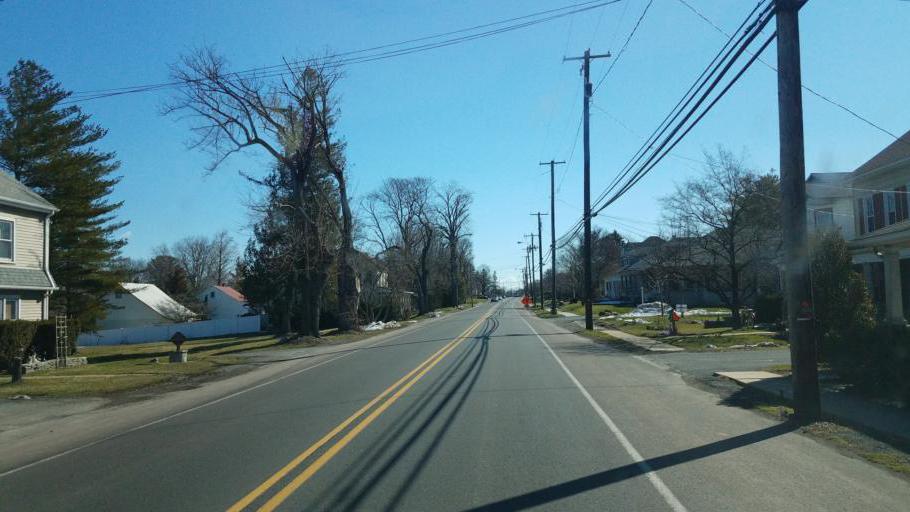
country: US
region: Pennsylvania
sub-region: Lancaster County
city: Brownstown
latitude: 40.0916
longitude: -76.1619
